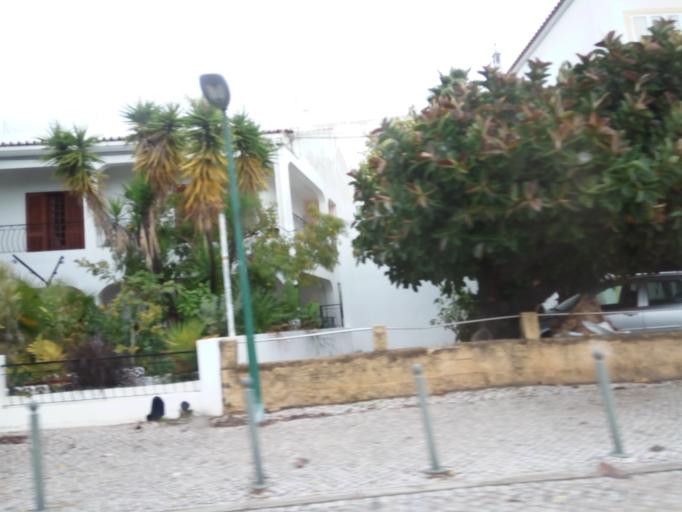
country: PT
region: Faro
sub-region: Loule
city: Loule
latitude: 37.1333
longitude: -8.0199
